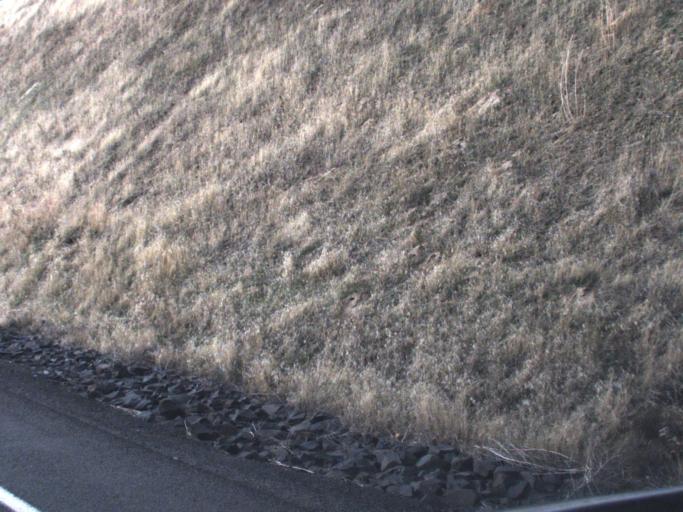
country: US
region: Washington
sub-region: Whitman County
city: Colfax
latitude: 46.8254
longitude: -117.5255
